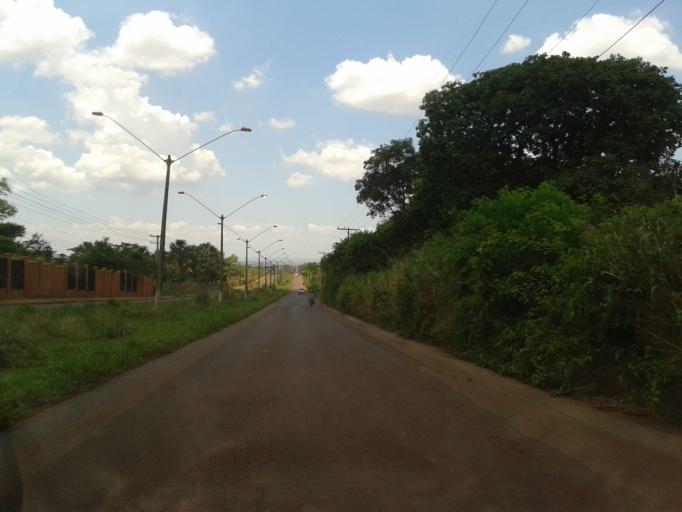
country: BR
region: Goias
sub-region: Itumbiara
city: Itumbiara
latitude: -18.3983
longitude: -49.2847
